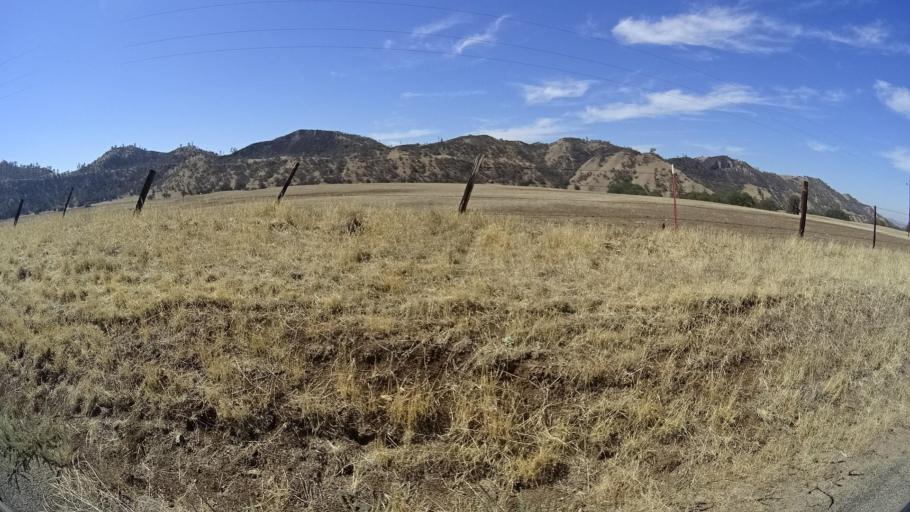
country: US
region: California
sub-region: Monterey County
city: King City
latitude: 36.1632
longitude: -120.7732
